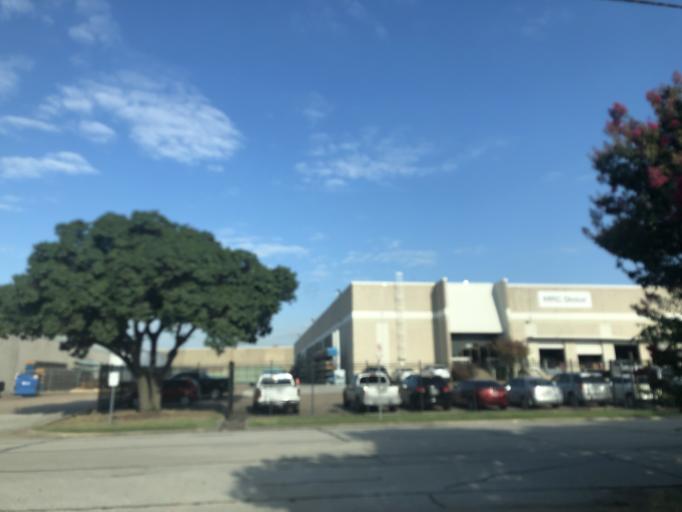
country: US
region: Texas
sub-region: Dallas County
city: Grand Prairie
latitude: 32.7331
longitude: -97.0400
